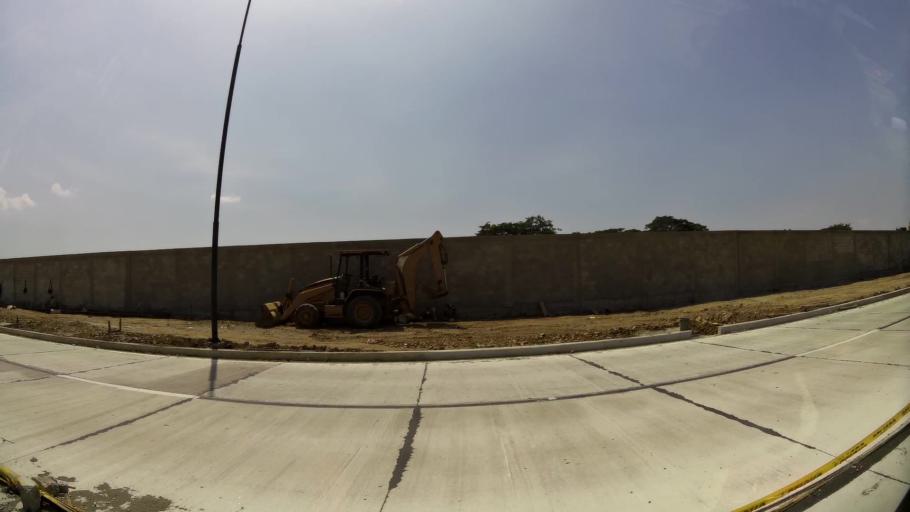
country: EC
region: Guayas
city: Eloy Alfaro
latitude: -2.0744
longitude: -79.8636
